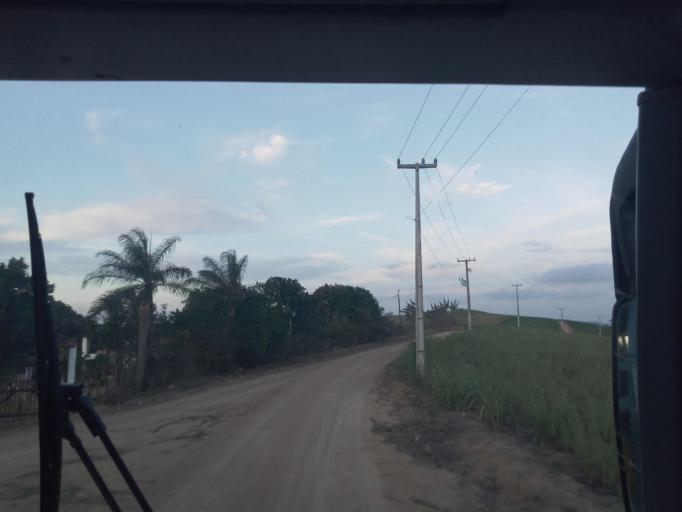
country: BR
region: Pernambuco
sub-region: Vitoria De Santo Antao
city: Vitoria de Santo Antao
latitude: -8.1568
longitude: -35.2526
